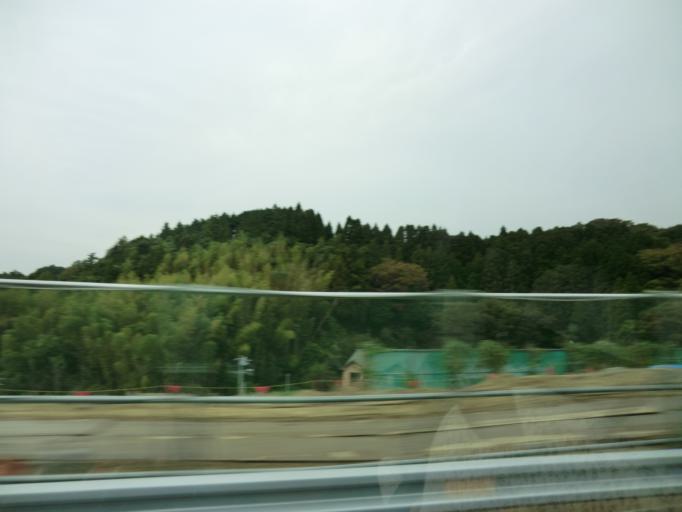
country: JP
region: Chiba
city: Kimitsu
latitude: 35.2646
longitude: 139.9011
